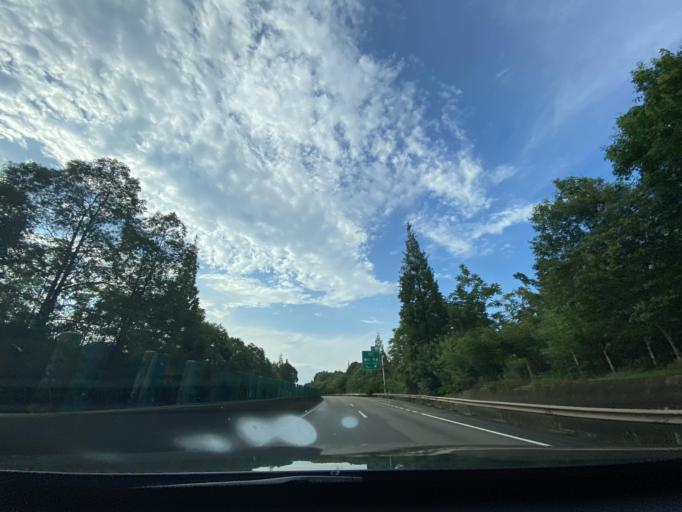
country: CN
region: Sichuan
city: Jiancheng
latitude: 30.2687
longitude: 104.6045
